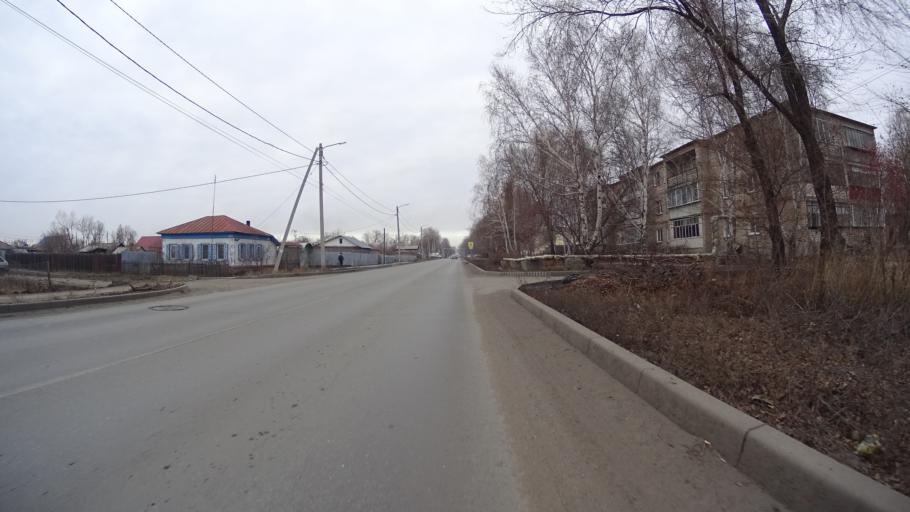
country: RU
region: Chelyabinsk
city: Troitsk
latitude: 54.1090
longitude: 61.5711
